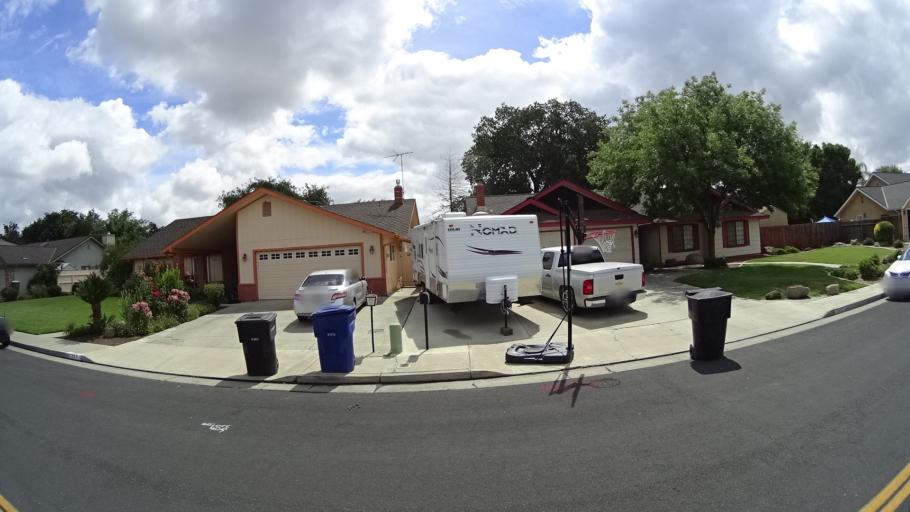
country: US
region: California
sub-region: Kings County
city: Hanford
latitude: 36.3379
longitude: -119.6645
